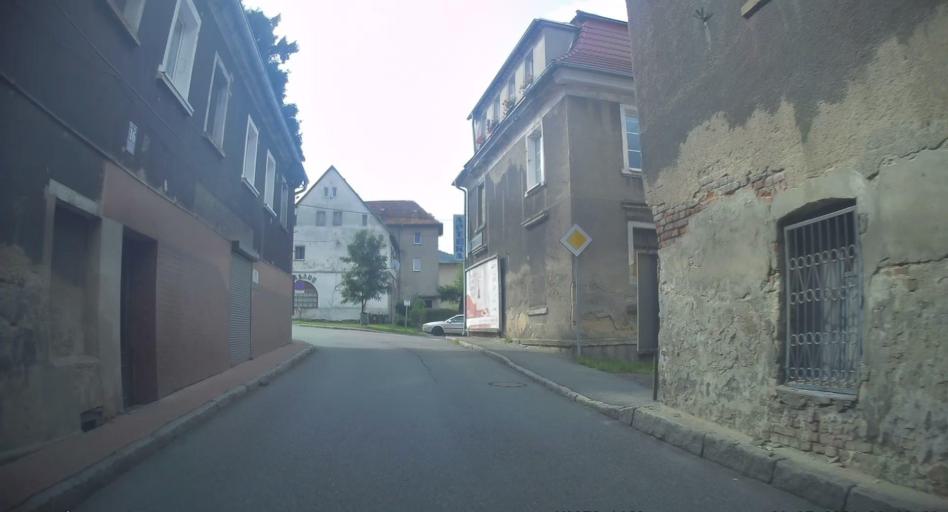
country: PL
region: Lower Silesian Voivodeship
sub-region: Powiat walbrzyski
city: Walim
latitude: 50.7001
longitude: 16.4403
